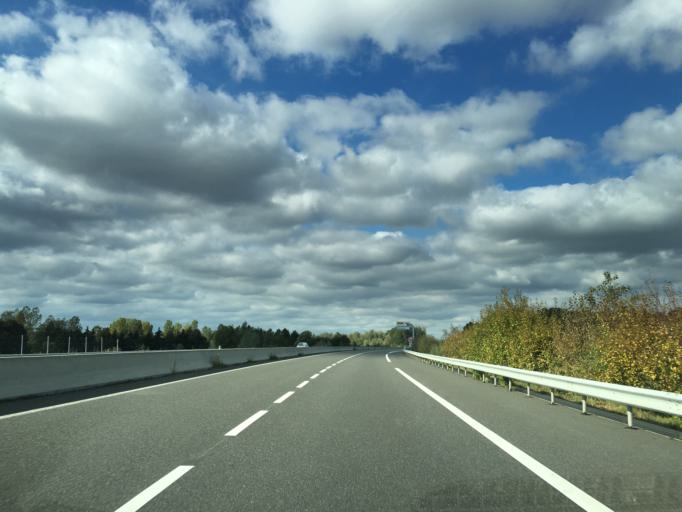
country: FR
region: Lorraine
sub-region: Departement de Meurthe-et-Moselle
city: Gerbeviller
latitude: 48.5343
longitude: 6.5794
